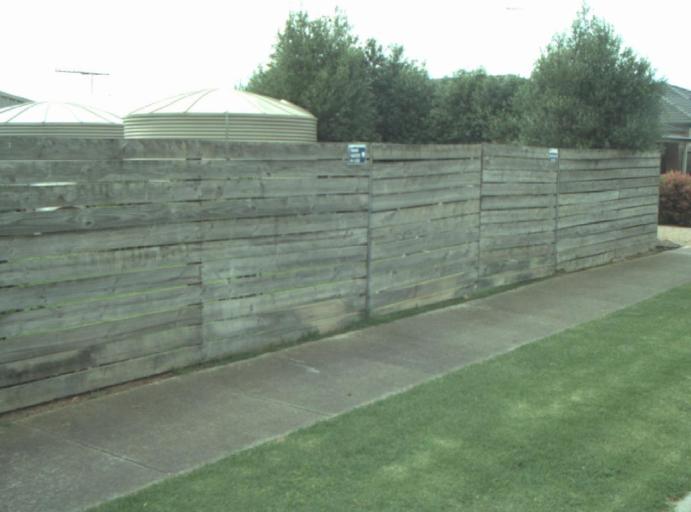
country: AU
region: Victoria
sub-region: Greater Geelong
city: Breakwater
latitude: -38.2034
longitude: 144.3454
